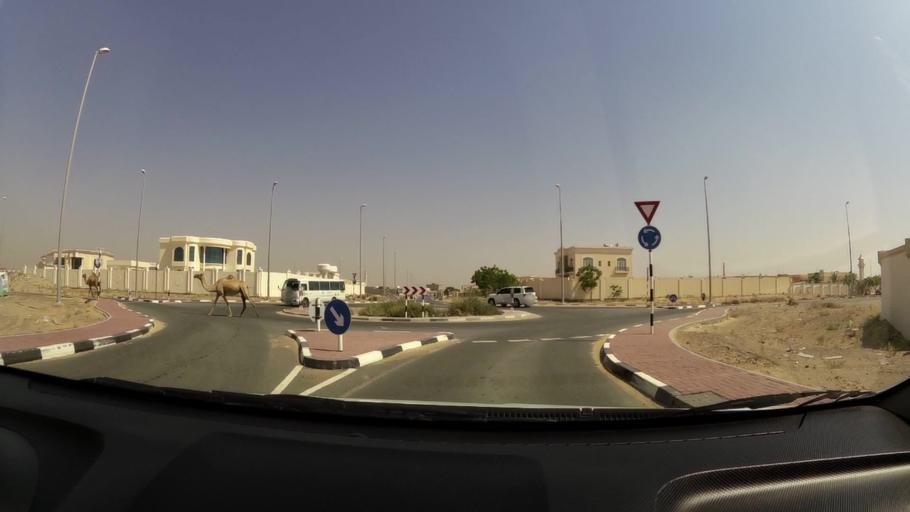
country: AE
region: Umm al Qaywayn
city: Umm al Qaywayn
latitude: 25.4873
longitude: 55.6030
